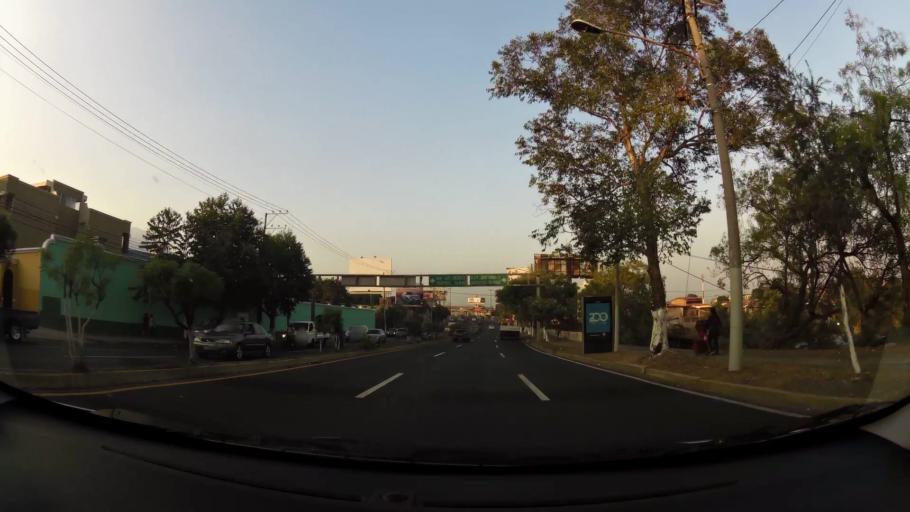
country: SV
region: San Salvador
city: San Salvador
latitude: 13.6897
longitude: -89.2173
